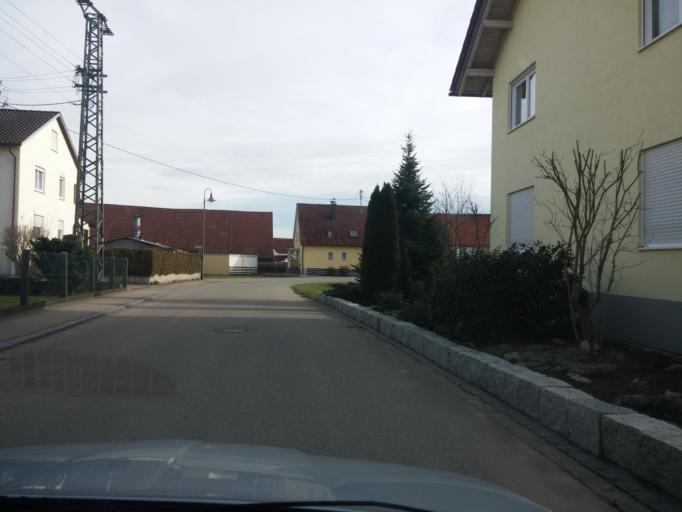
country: DE
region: Bavaria
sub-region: Swabia
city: Holzgunz
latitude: 48.0185
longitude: 10.2456
